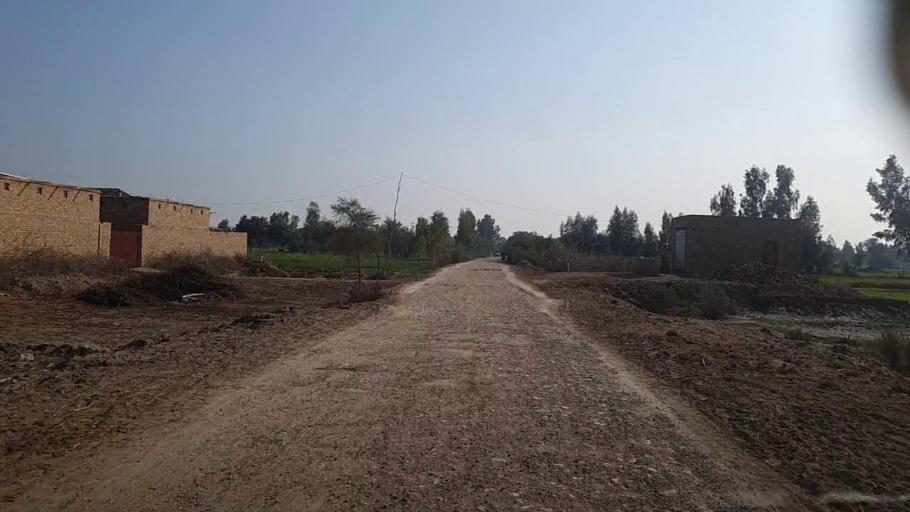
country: PK
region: Sindh
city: Mirpur Mathelo
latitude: 27.8872
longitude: 69.6104
